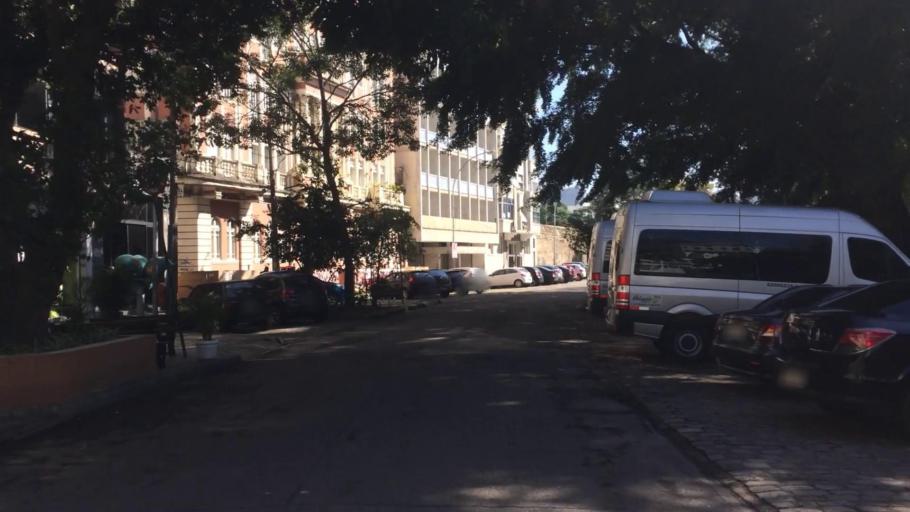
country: BR
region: Rio de Janeiro
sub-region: Rio De Janeiro
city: Rio de Janeiro
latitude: -22.9218
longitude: -43.1744
